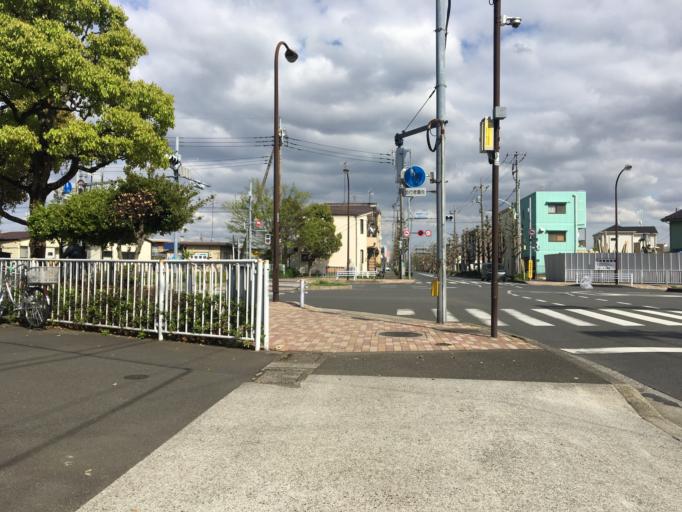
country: JP
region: Tokyo
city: Chofugaoka
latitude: 35.6463
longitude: 139.5091
